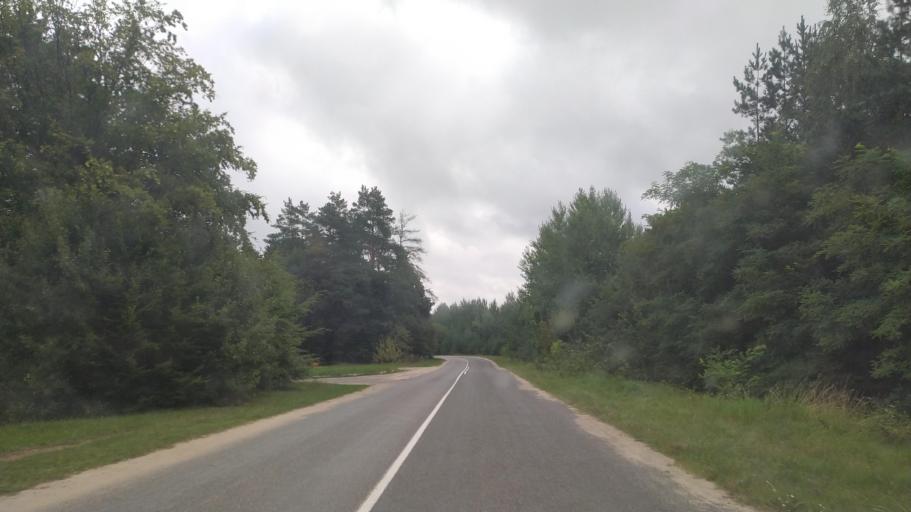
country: BY
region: Brest
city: Byaroza
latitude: 52.5991
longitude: 24.8763
